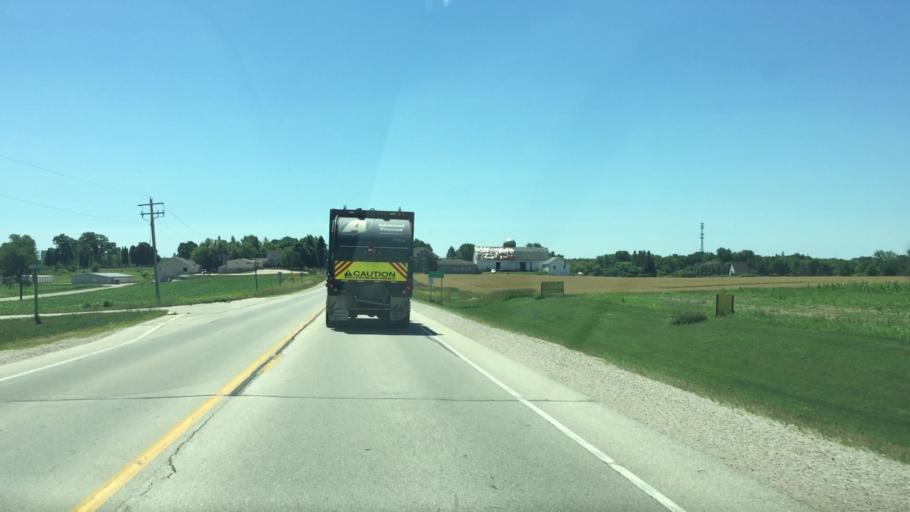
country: US
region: Wisconsin
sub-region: Calumet County
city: Chilton
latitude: 44.0456
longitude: -88.1630
